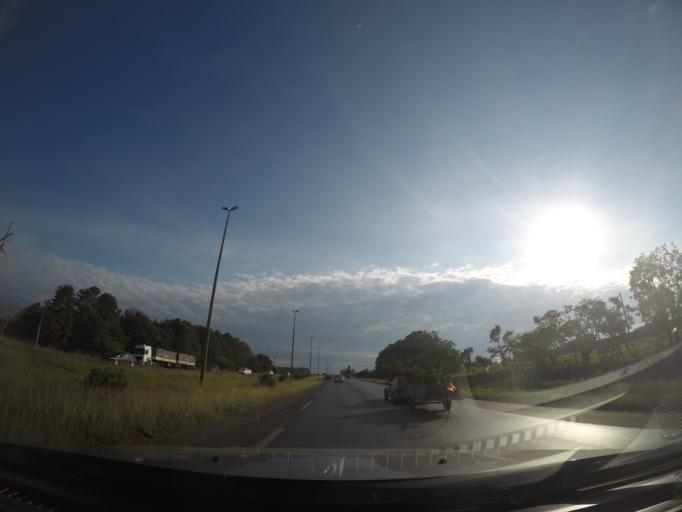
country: BR
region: Federal District
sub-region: Brasilia
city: Brasilia
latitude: -15.6420
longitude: -47.7561
